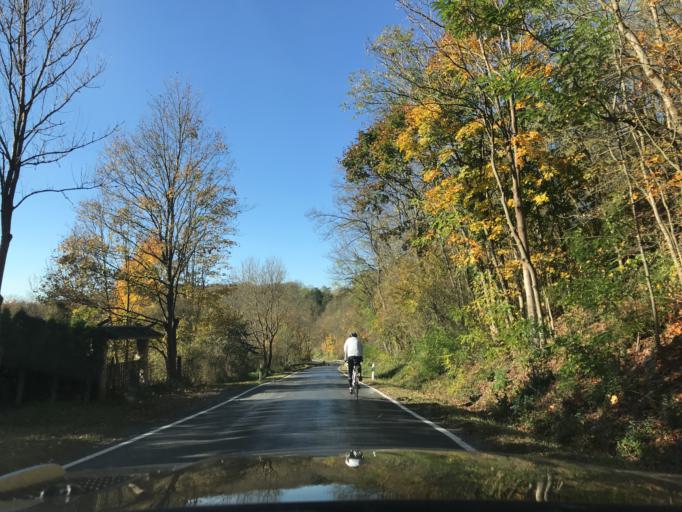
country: DE
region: Thuringia
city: Sollstedt
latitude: 51.2712
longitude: 10.4388
